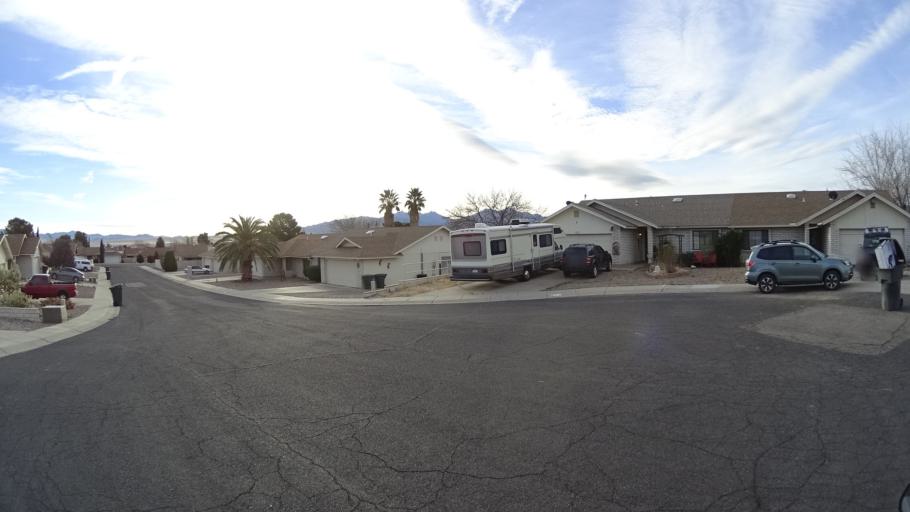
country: US
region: Arizona
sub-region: Mohave County
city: New Kingman-Butler
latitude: 35.2402
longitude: -114.0428
